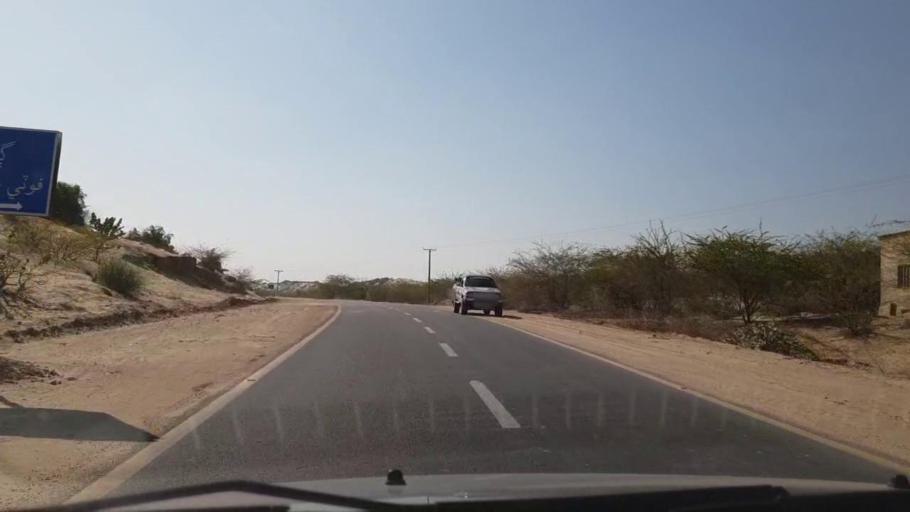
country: PK
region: Sindh
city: Diplo
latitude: 24.4907
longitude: 69.5918
